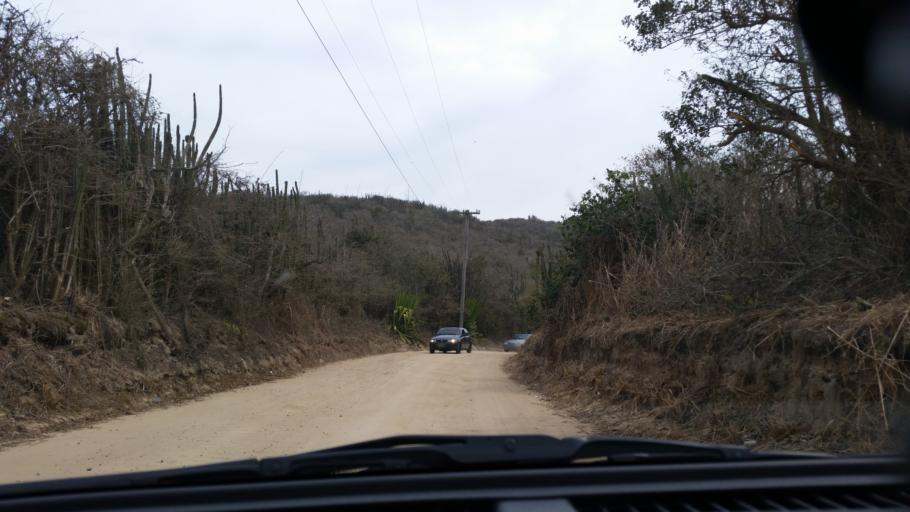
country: BR
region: Rio de Janeiro
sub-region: Cabo Frio
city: Cabo Frio
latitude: -22.8738
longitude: -41.9867
